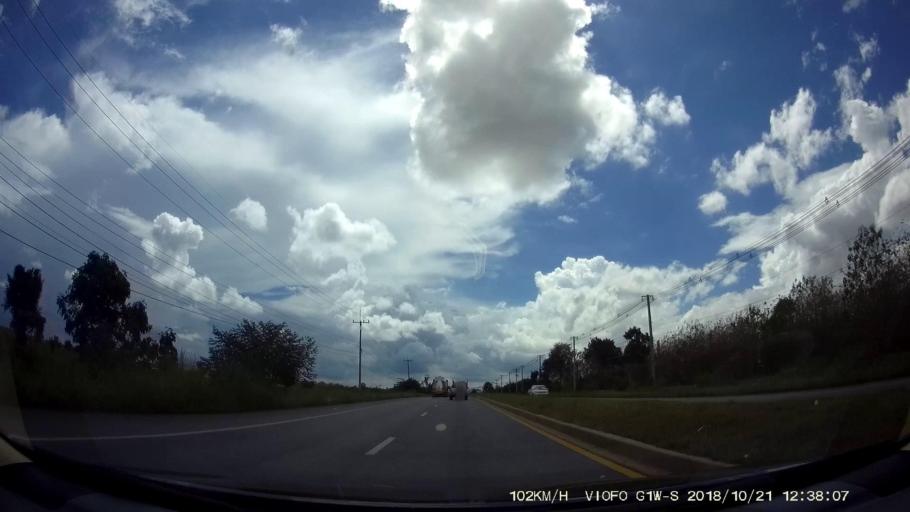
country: TH
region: Nakhon Ratchasima
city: Amphoe Sikhiu
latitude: 15.0588
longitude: 101.7077
